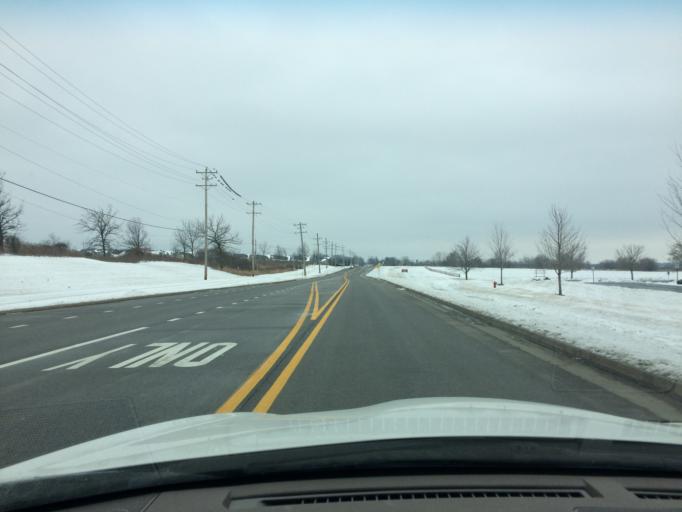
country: US
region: Illinois
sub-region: Kane County
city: Village of Campton Hills
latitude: 41.9008
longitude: -88.3594
